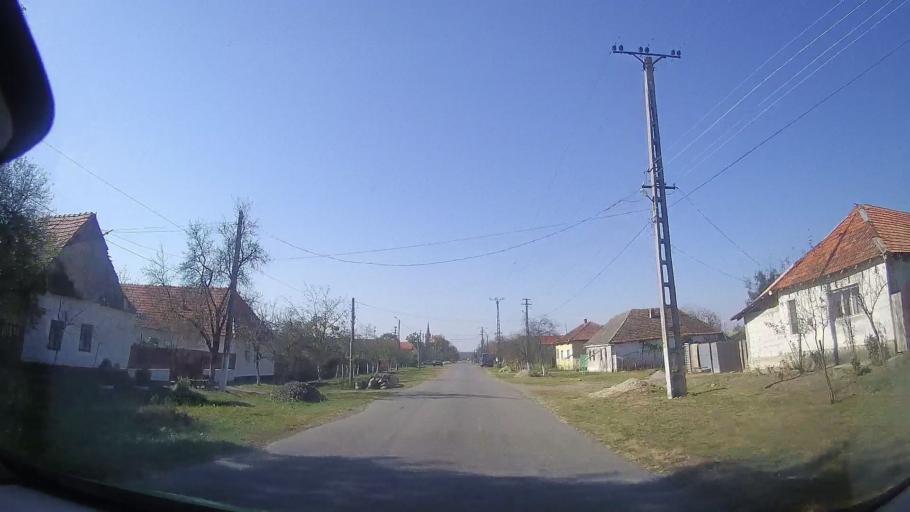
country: RO
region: Timis
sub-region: Comuna Ghizela
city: Ghizela
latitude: 45.8236
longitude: 21.7492
